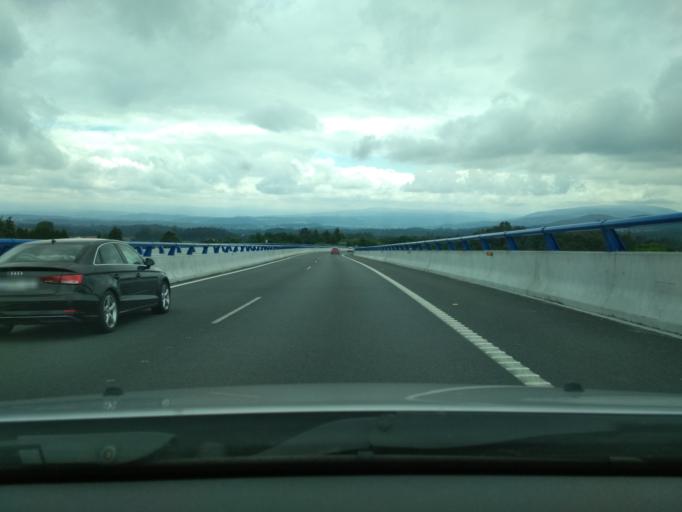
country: ES
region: Galicia
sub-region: Provincia da Coruna
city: Santiago de Compostela
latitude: 42.8331
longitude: -8.5726
